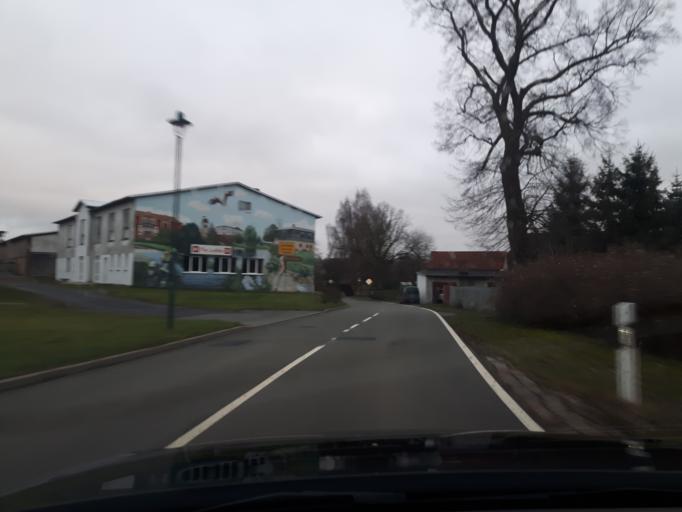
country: DE
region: Mecklenburg-Vorpommern
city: Bad Sulze
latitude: 54.0483
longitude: 12.6891
